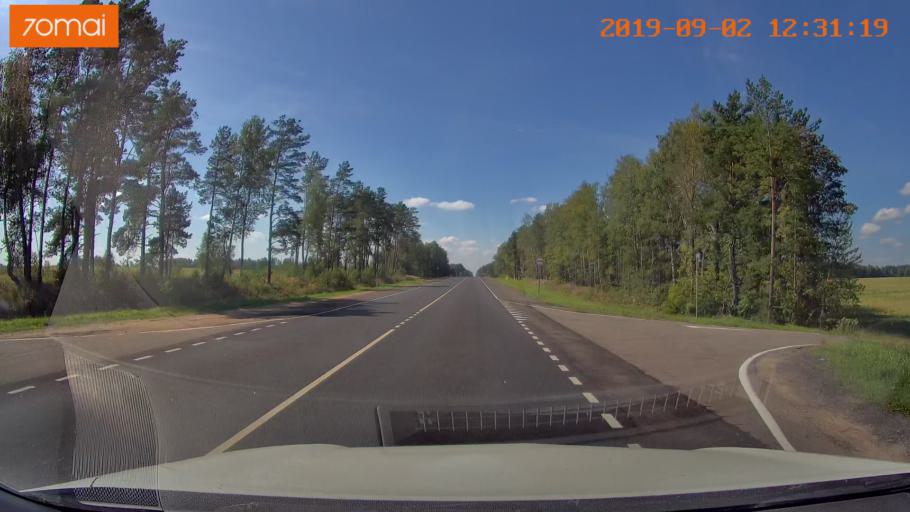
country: RU
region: Smolensk
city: Shumyachi
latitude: 53.8255
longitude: 32.4532
